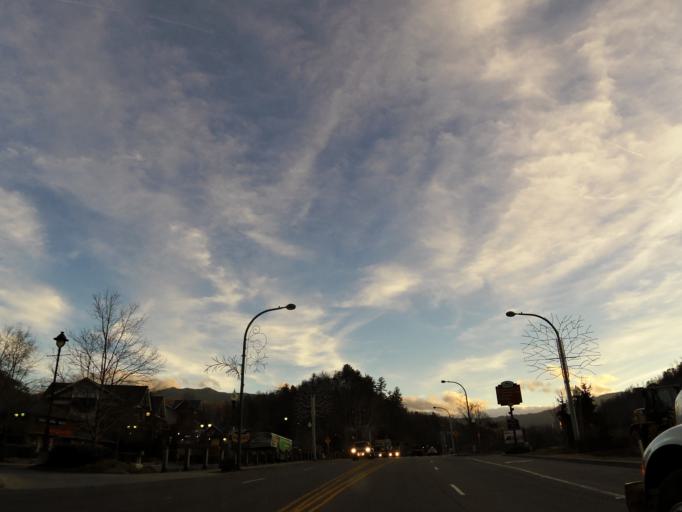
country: US
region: Tennessee
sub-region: Sevier County
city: Gatlinburg
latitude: 35.7252
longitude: -83.5103
